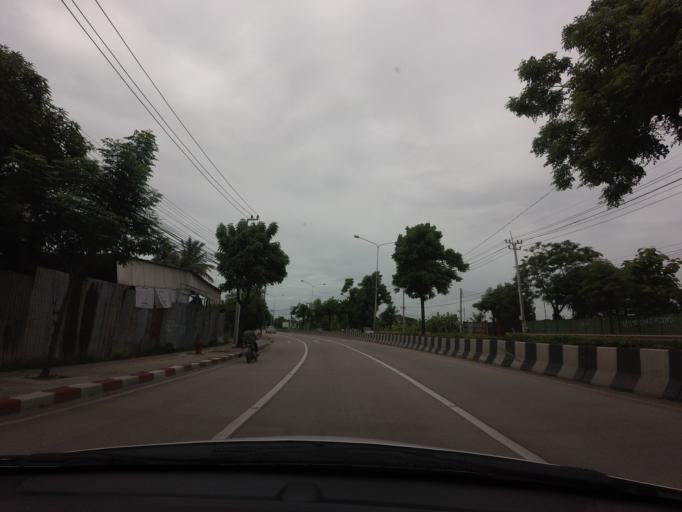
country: TH
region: Pathum Thani
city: Lam Luk Ka
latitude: 13.9108
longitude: 100.7460
